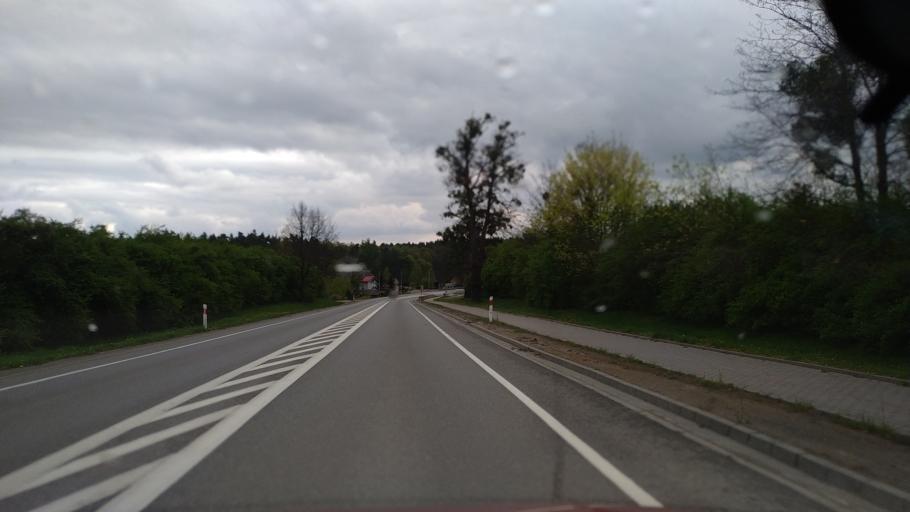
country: PL
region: Pomeranian Voivodeship
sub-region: Powiat tczewski
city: Subkowy
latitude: 54.0429
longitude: 18.7010
